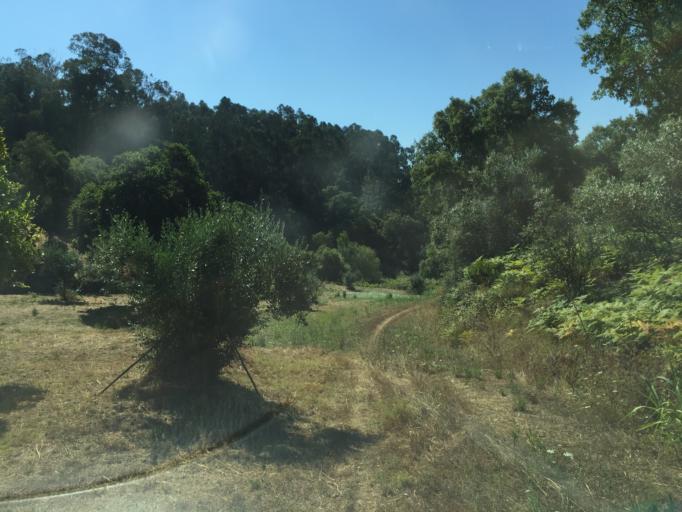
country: PT
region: Santarem
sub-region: Tomar
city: Tomar
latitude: 39.6054
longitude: -8.3473
